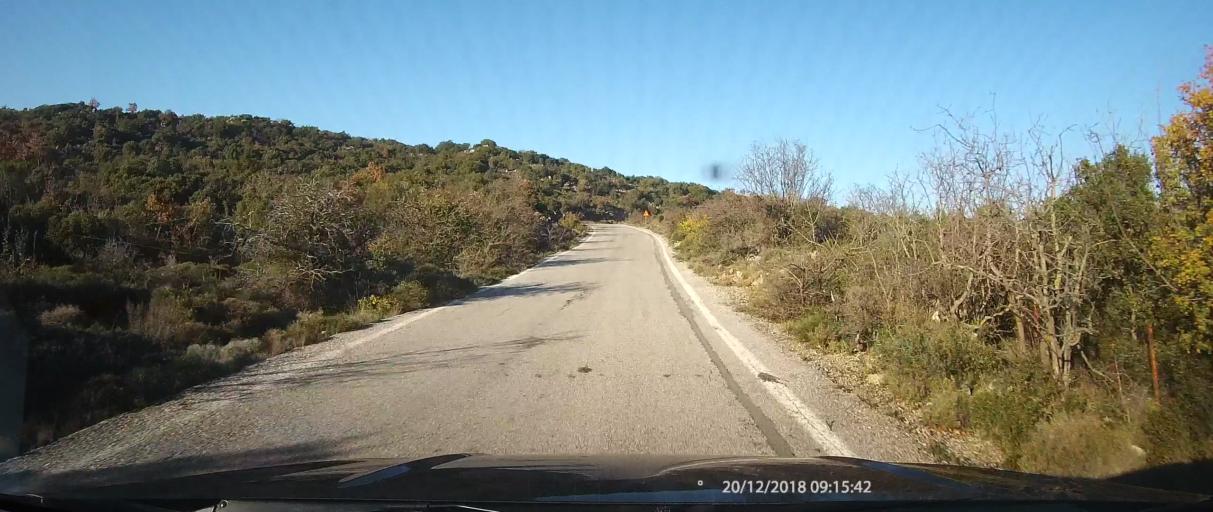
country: GR
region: Peloponnese
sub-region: Nomos Lakonias
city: Sykea
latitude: 36.9008
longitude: 22.9760
